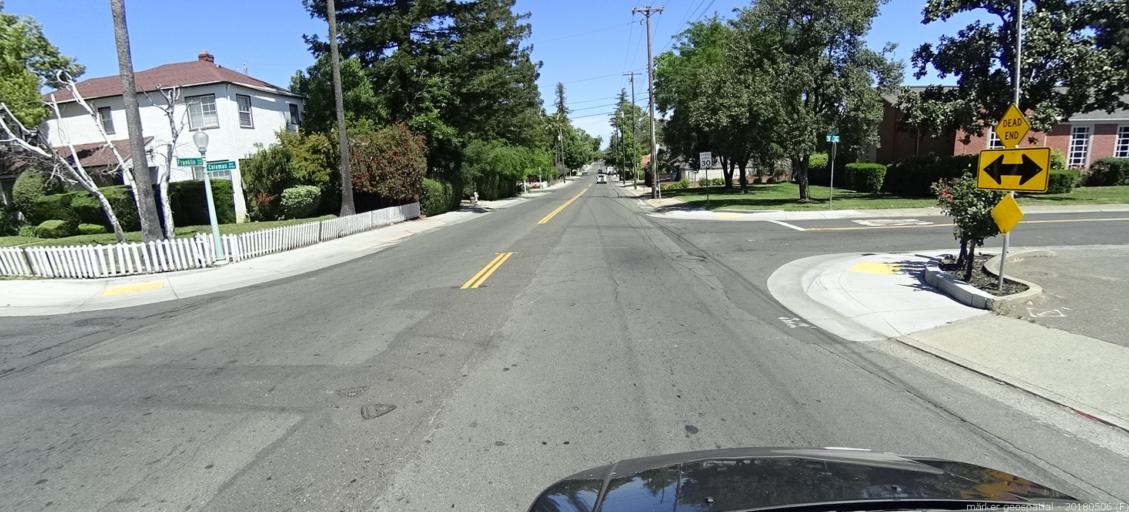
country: US
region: California
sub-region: Sacramento County
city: Sacramento
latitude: 38.5416
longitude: -121.4758
